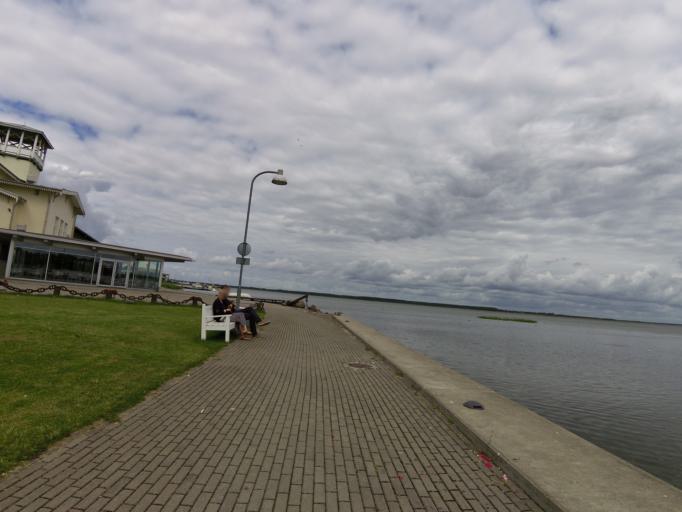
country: EE
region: Laeaene
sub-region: Haapsalu linn
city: Haapsalu
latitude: 58.9535
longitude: 23.5324
